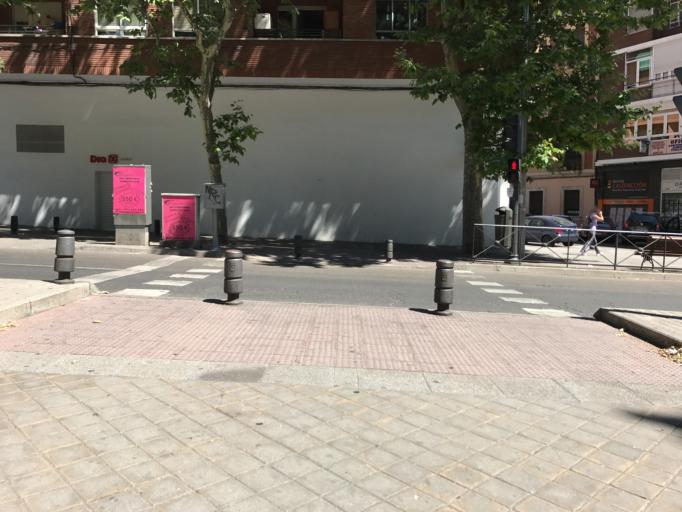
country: ES
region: Madrid
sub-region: Provincia de Madrid
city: Arganzuela
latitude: 40.4050
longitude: -3.6957
